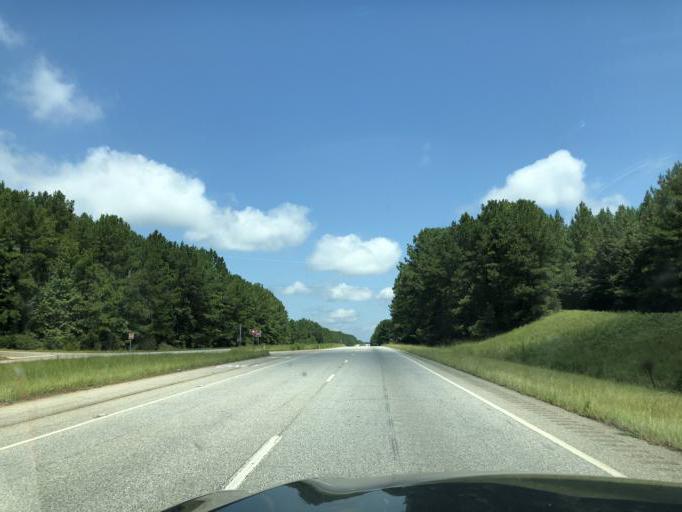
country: US
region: Alabama
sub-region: Henry County
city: Abbeville
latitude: 31.6540
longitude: -85.2802
